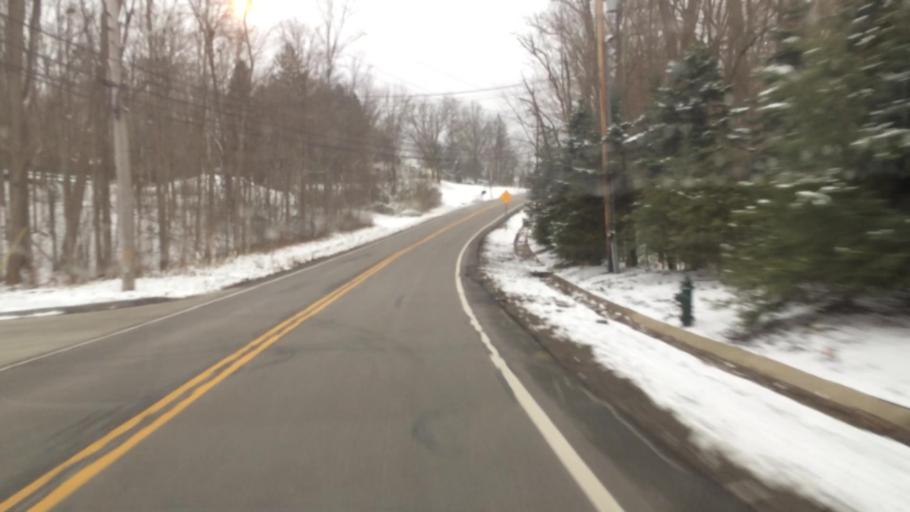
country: US
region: Ohio
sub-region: Cuyahoga County
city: Strongsville
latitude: 41.3177
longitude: -81.7912
